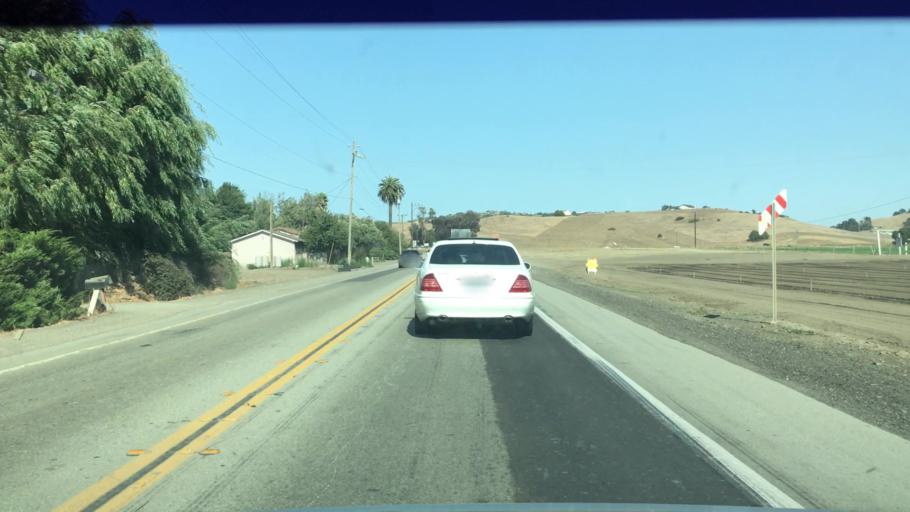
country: US
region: California
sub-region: San Benito County
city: Hollister
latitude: 36.8417
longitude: -121.4642
